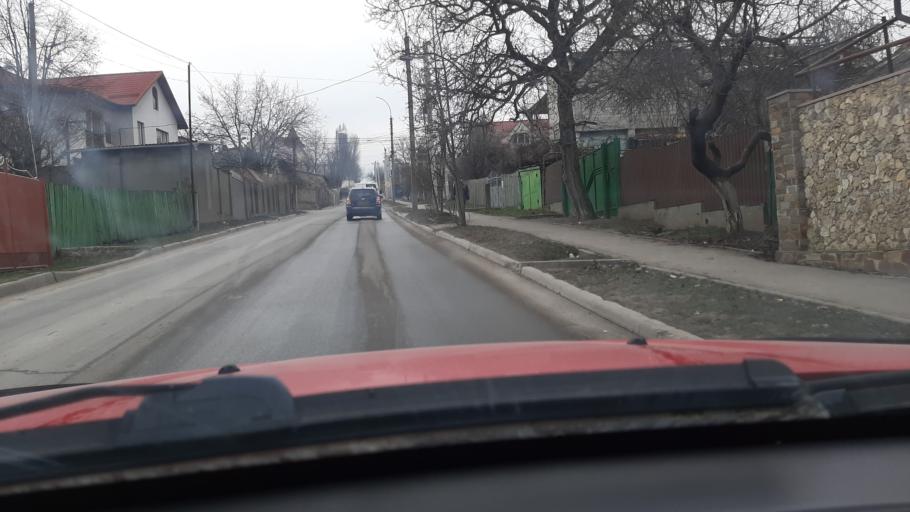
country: MD
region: Chisinau
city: Vatra
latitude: 47.0407
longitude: 28.7935
